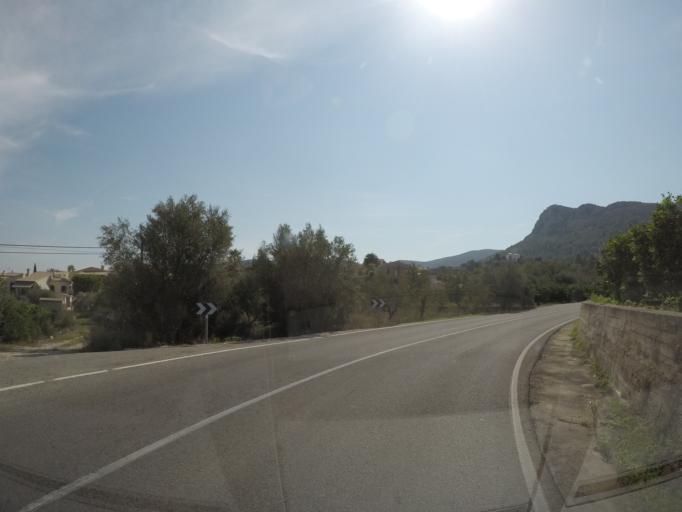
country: ES
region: Valencia
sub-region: Provincia de Alicante
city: Orba
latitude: 38.7814
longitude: -0.0740
